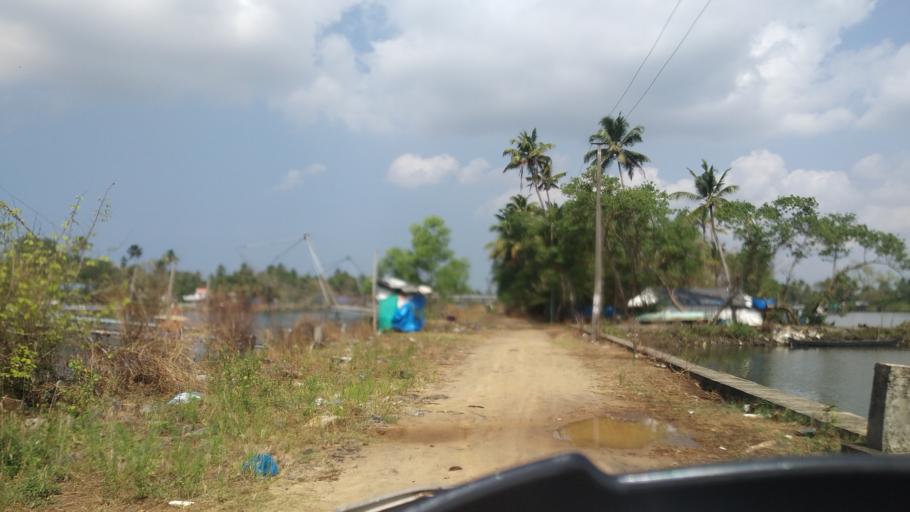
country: IN
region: Kerala
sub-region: Thrissur District
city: Kodungallur
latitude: 10.1377
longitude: 76.2048
